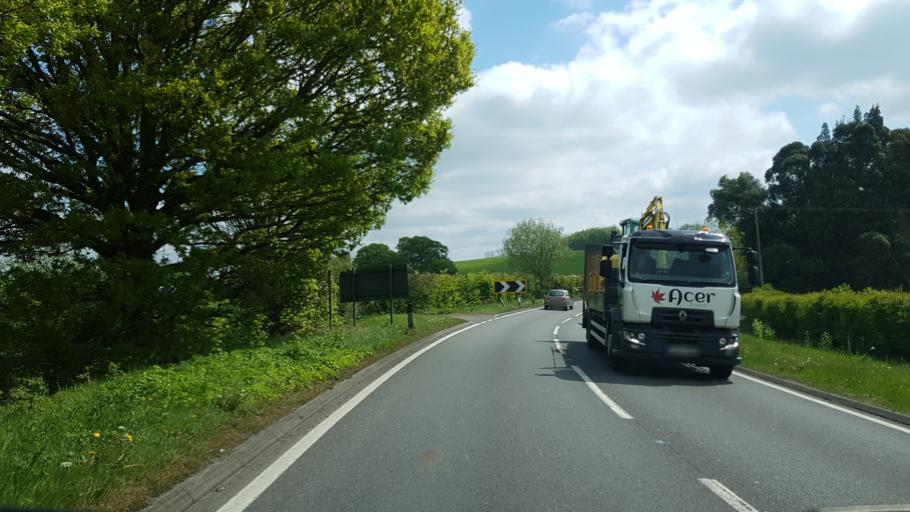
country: GB
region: England
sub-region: Kent
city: Paddock Wood
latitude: 51.1173
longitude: 0.3818
